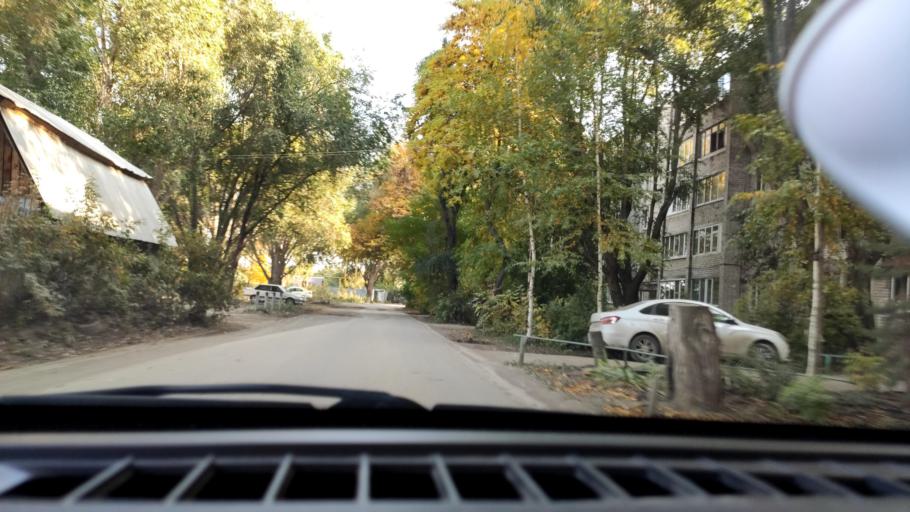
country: RU
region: Samara
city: Smyshlyayevka
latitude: 53.1901
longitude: 50.2803
